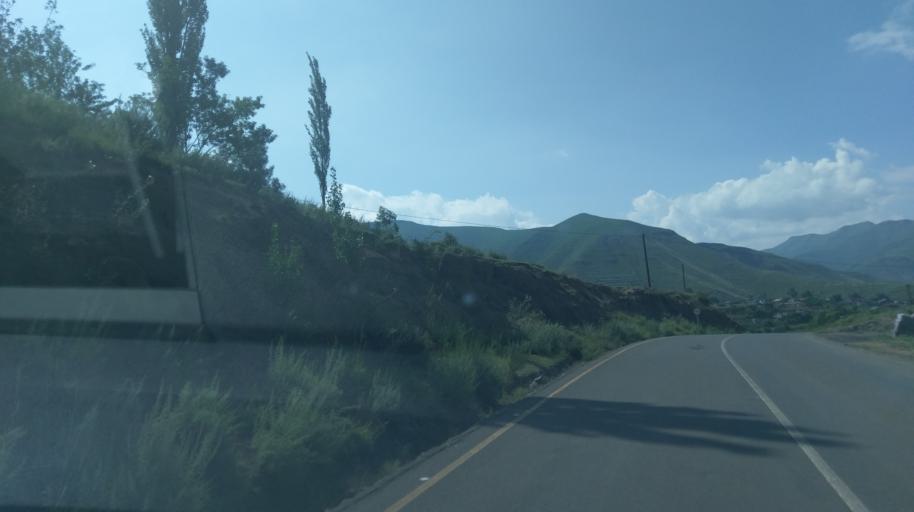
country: LS
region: Thaba-Tseka
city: Thaba-Tseka
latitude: -29.1159
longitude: 28.4910
